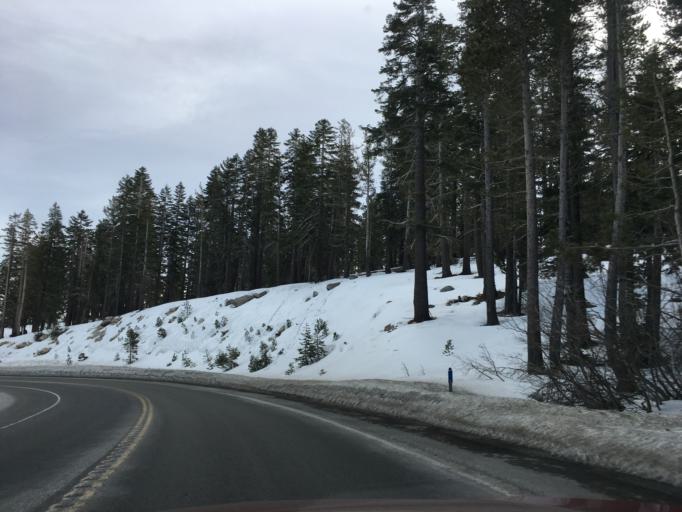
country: US
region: Nevada
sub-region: Washoe County
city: Incline Village
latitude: 39.3281
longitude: -119.8833
